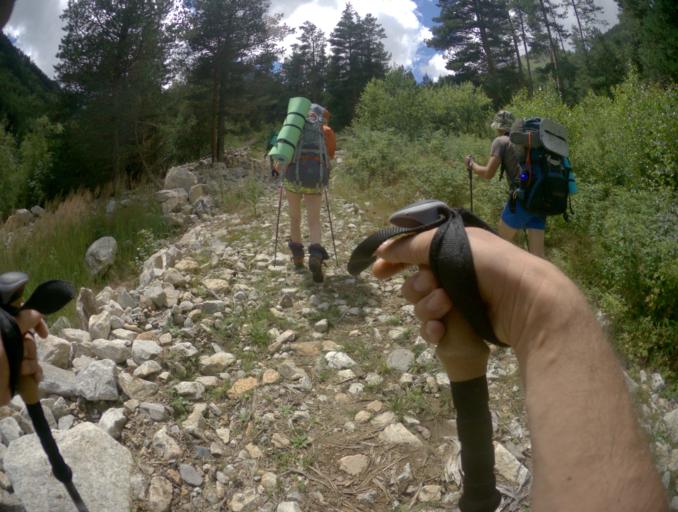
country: RU
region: Karachayevo-Cherkesiya
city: Uchkulan
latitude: 43.3507
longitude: 42.1585
